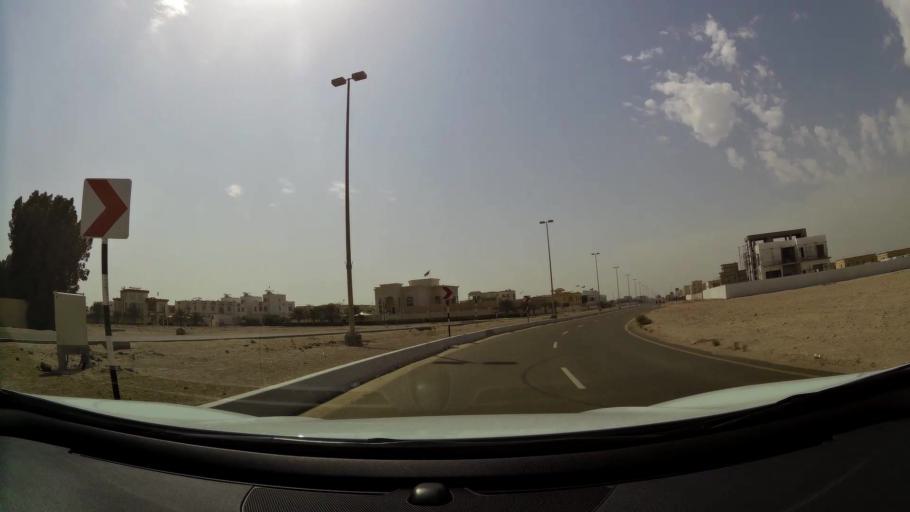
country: AE
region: Abu Dhabi
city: Abu Dhabi
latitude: 24.3327
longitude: 54.5659
